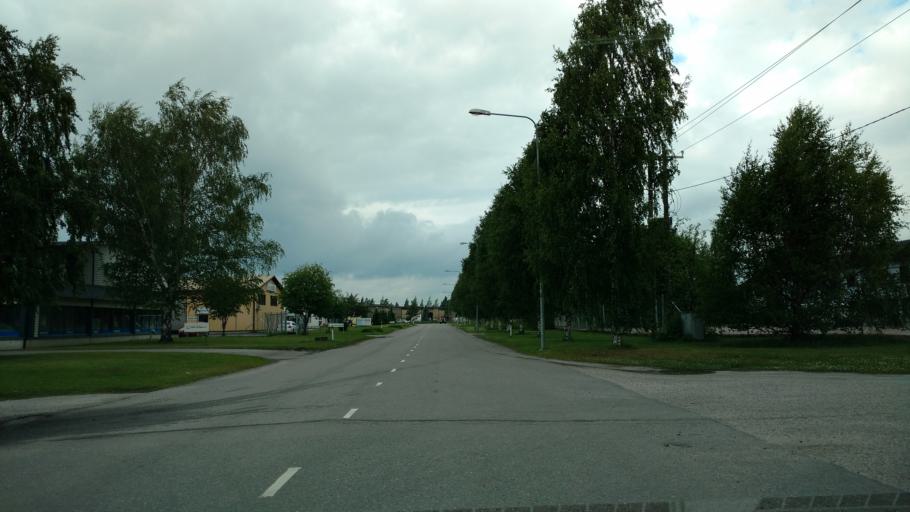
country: FI
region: Varsinais-Suomi
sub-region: Salo
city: Salo
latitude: 60.3801
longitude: 23.1080
